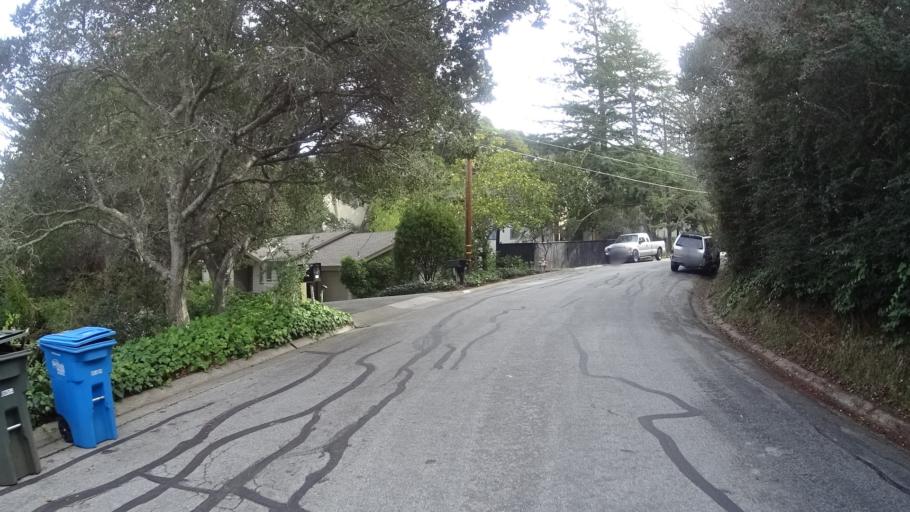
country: US
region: California
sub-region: San Mateo County
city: Hillsborough
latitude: 37.5713
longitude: -122.3912
